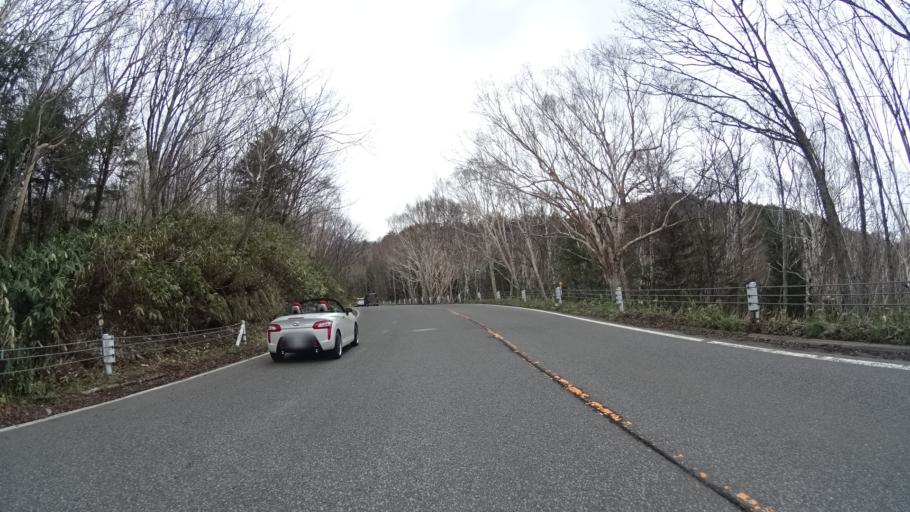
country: JP
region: Nagano
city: Nakano
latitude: 36.7089
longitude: 138.4890
